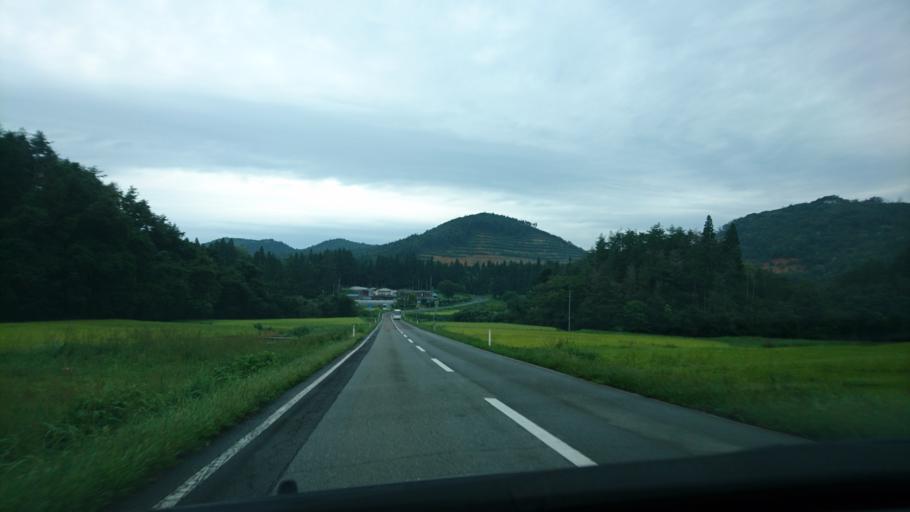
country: JP
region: Iwate
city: Ichinoseki
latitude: 39.0249
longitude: 141.2026
